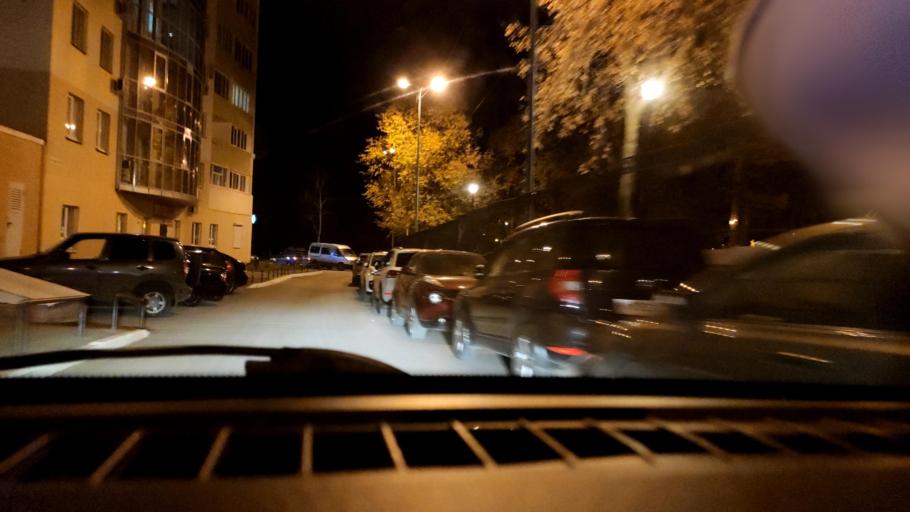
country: RU
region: Samara
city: Samara
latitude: 53.1945
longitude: 50.2054
